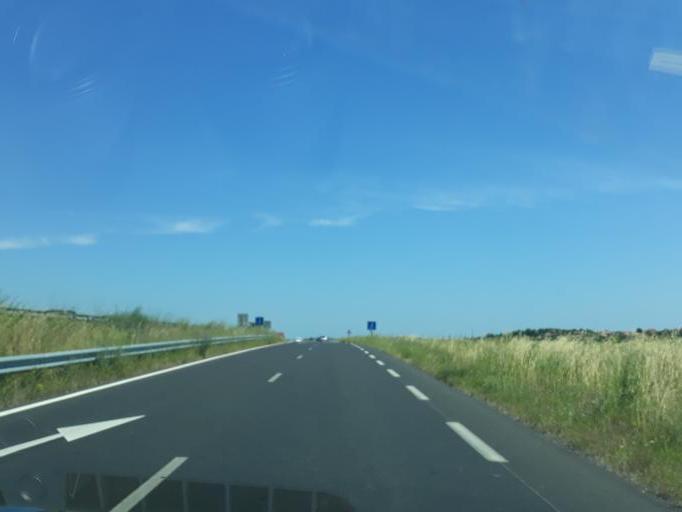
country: FR
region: Languedoc-Roussillon
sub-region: Departement de l'Herault
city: Portiragnes
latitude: 43.3137
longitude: 3.3223
